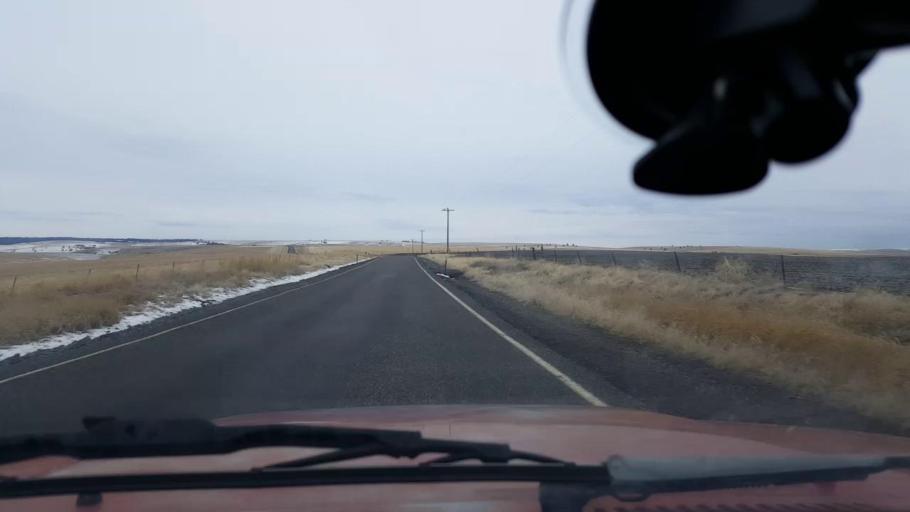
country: US
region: Washington
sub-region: Asotin County
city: Clarkston Heights-Vineland
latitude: 46.3238
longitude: -117.3596
